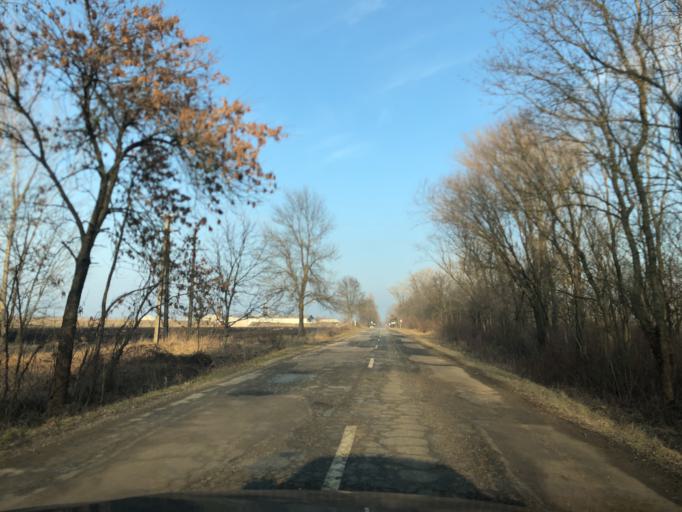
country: HU
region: Gyor-Moson-Sopron
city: Kapuvar
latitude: 47.5788
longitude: 17.0805
